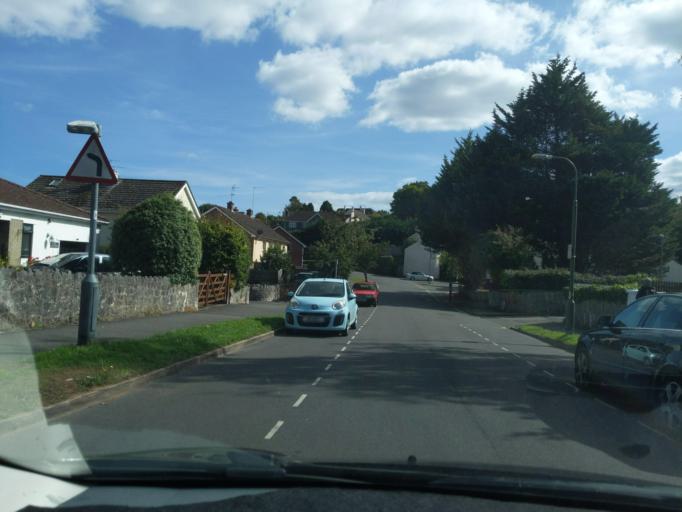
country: GB
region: England
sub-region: Devon
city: Kingskerswell
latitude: 50.4792
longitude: -3.5621
